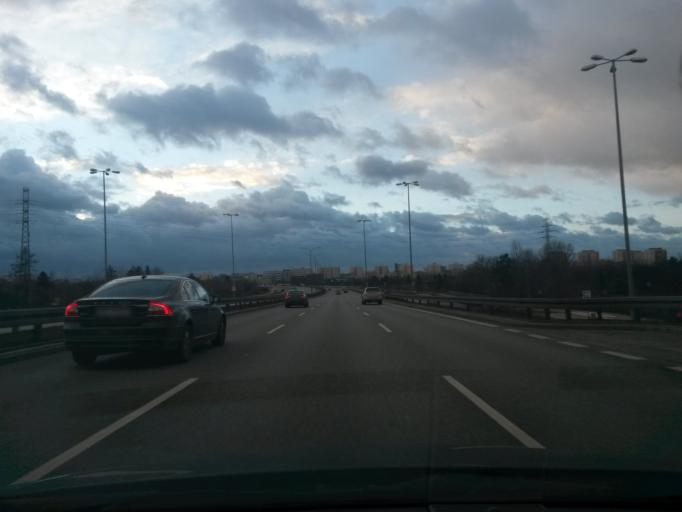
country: PL
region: Masovian Voivodeship
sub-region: Warszawa
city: Mokotow
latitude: 52.2030
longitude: 21.0679
